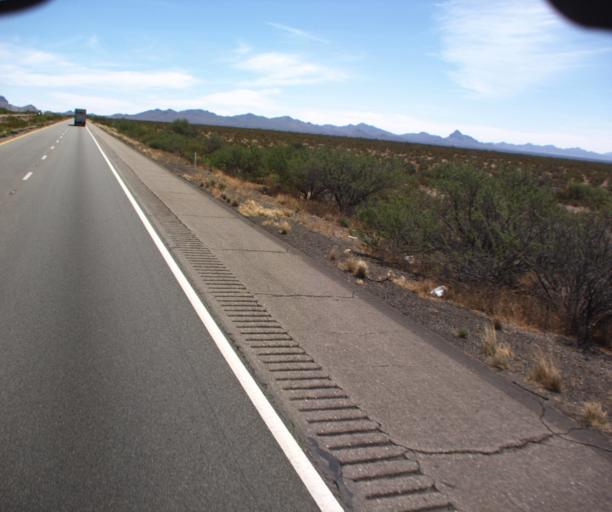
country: US
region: New Mexico
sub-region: Hidalgo County
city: Lordsburg
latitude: 32.2474
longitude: -109.1357
